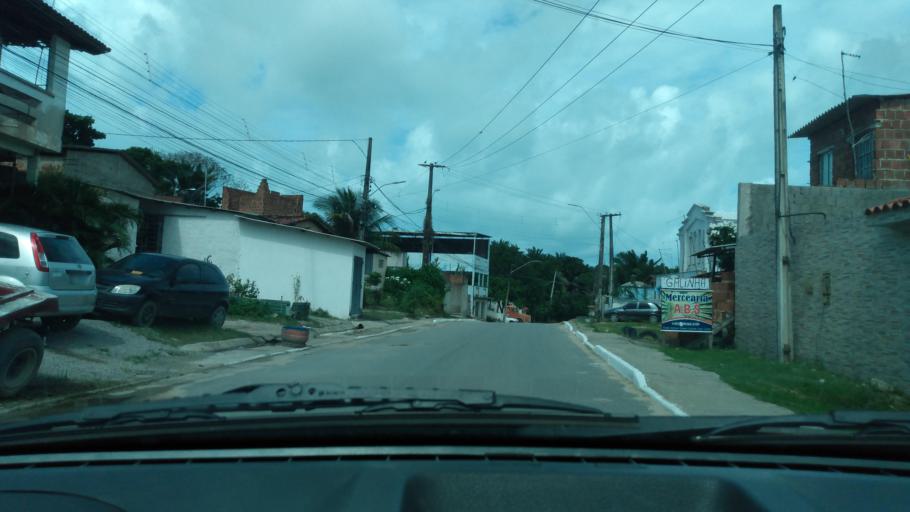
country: BR
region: Pernambuco
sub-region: Cabo De Santo Agostinho
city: Cabo
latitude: -8.3459
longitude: -34.9609
